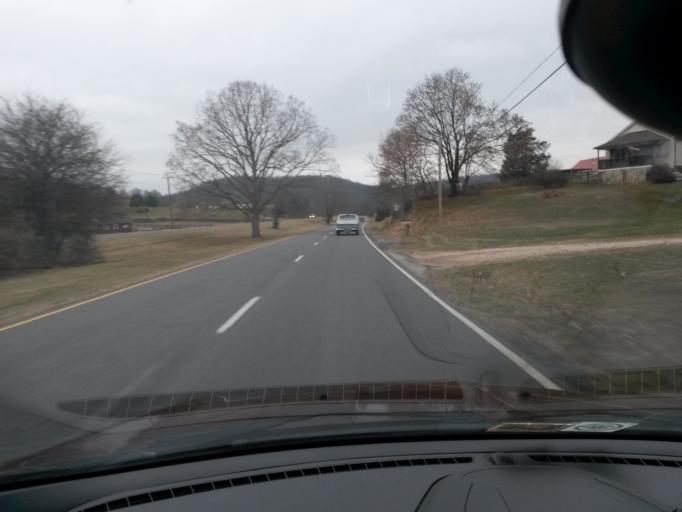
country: US
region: Virginia
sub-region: City of Buena Vista
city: Buena Vista
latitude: 37.9004
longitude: -79.2492
